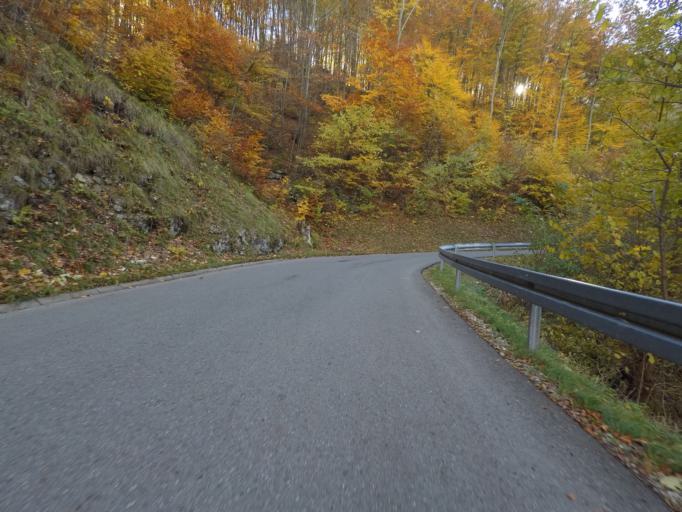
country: DE
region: Baden-Wuerttemberg
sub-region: Tuebingen Region
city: Pfullingen
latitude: 48.4180
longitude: 9.2408
